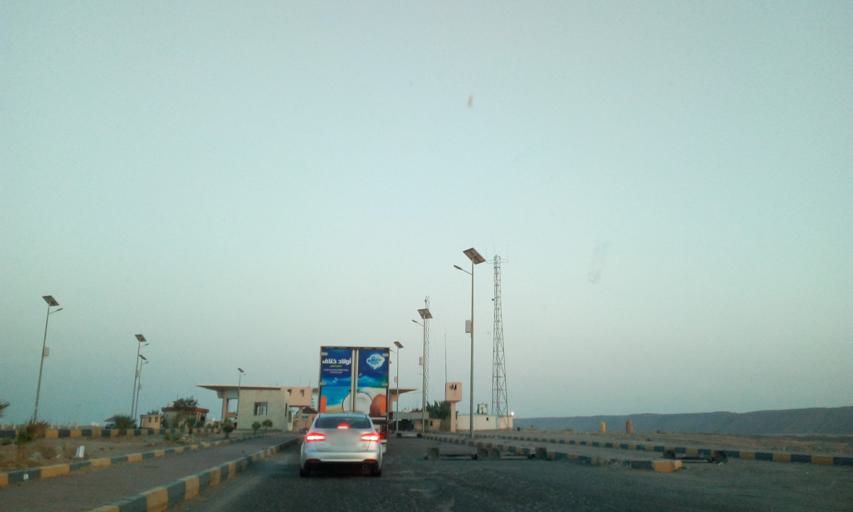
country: EG
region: Red Sea
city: El Gouna
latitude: 27.4211
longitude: 33.6148
